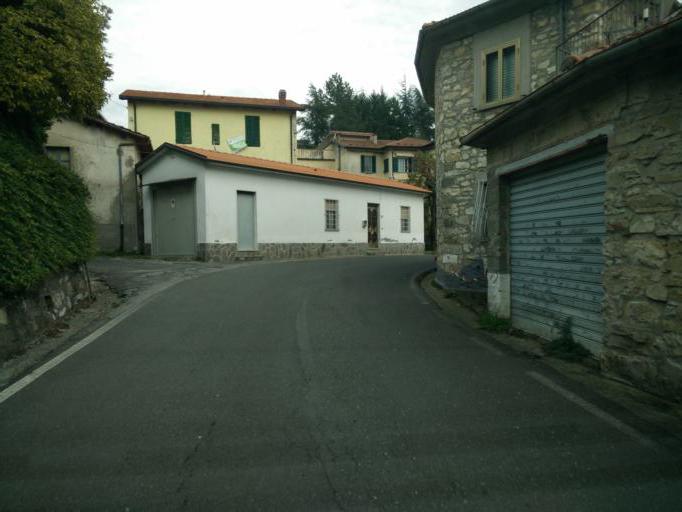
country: IT
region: Tuscany
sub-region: Provincia di Massa-Carrara
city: Casola in Lunigiana
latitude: 44.2115
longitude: 10.1829
